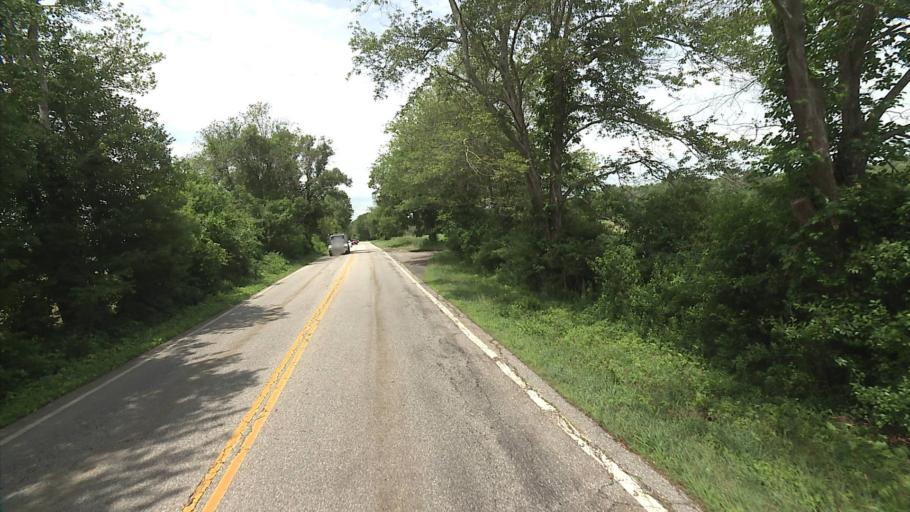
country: US
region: Connecticut
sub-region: New London County
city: Jewett City
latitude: 41.5732
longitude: -71.9716
